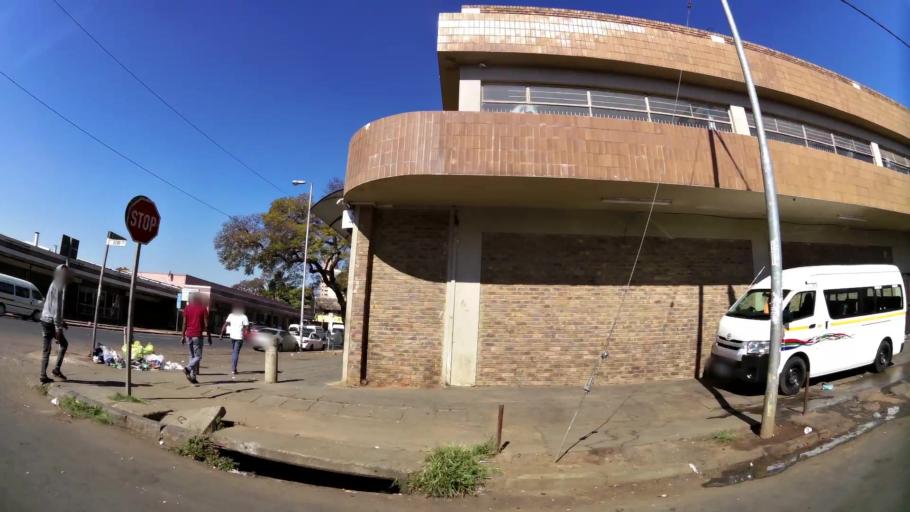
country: ZA
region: Gauteng
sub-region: City of Tshwane Metropolitan Municipality
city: Pretoria
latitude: -25.7409
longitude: 28.1949
